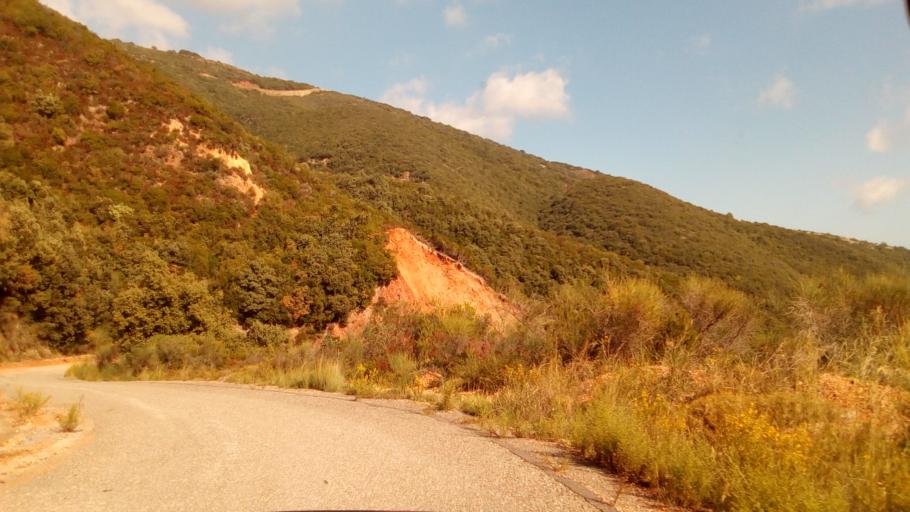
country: GR
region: West Greece
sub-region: Nomos Aitolias kai Akarnanias
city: Nafpaktos
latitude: 38.4202
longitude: 21.8521
